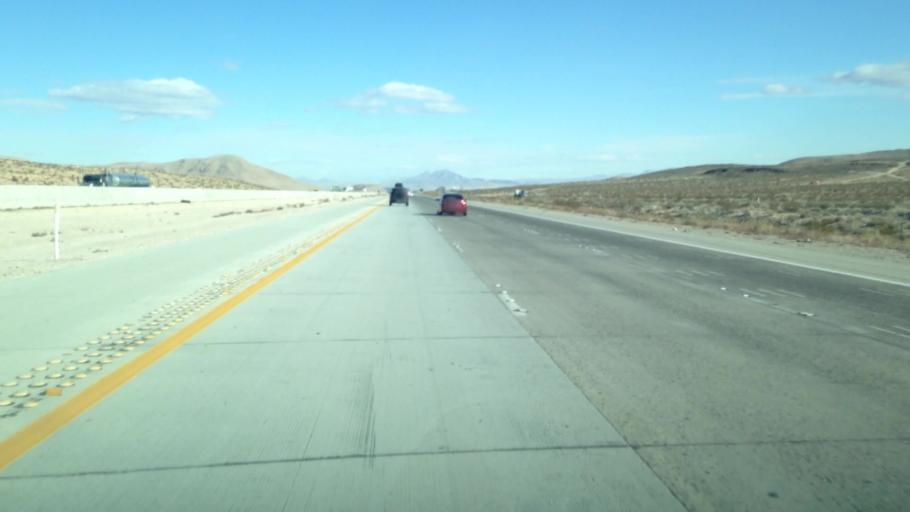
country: US
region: Nevada
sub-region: Clark County
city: Enterprise
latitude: 35.9018
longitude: -115.2132
